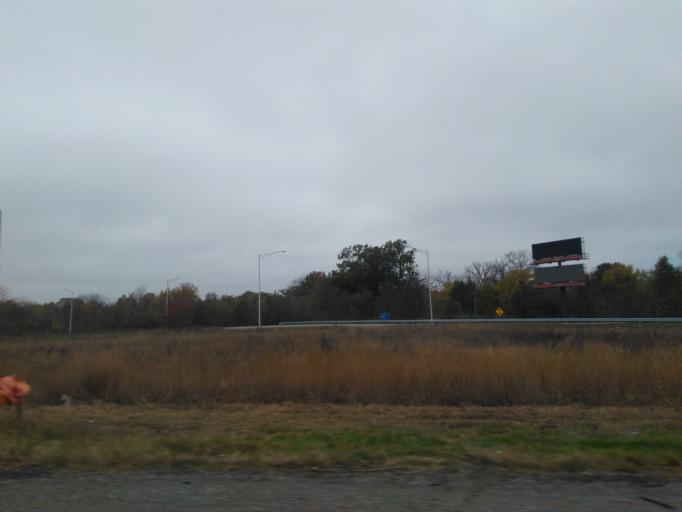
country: US
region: Illinois
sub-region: Saint Clair County
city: Washington Park
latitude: 38.6045
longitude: -90.0847
